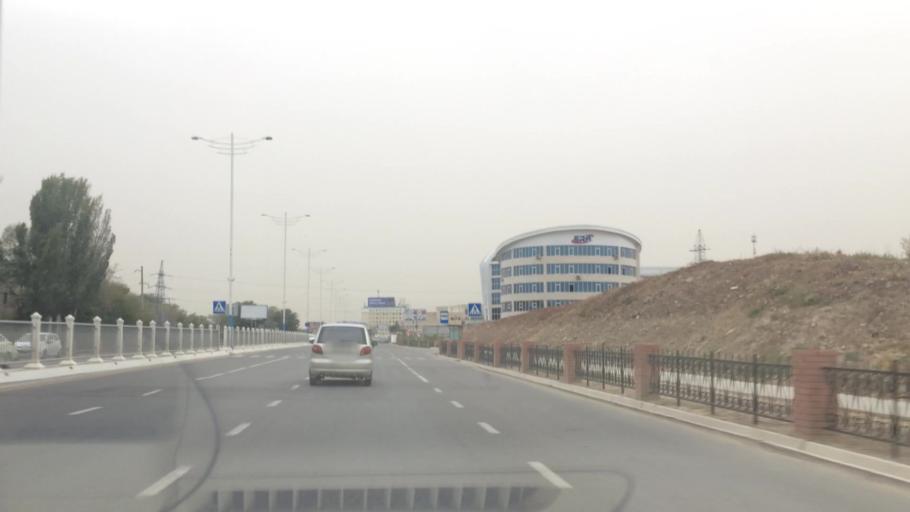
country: UZ
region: Toshkent
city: Salor
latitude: 41.3041
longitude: 69.3132
